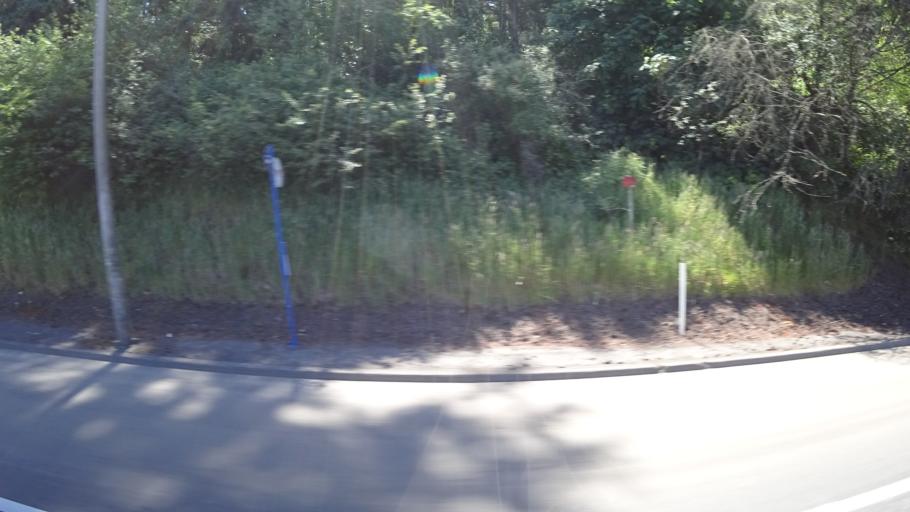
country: US
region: Oregon
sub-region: Washington County
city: Oak Hills
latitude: 45.6102
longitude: -122.7957
